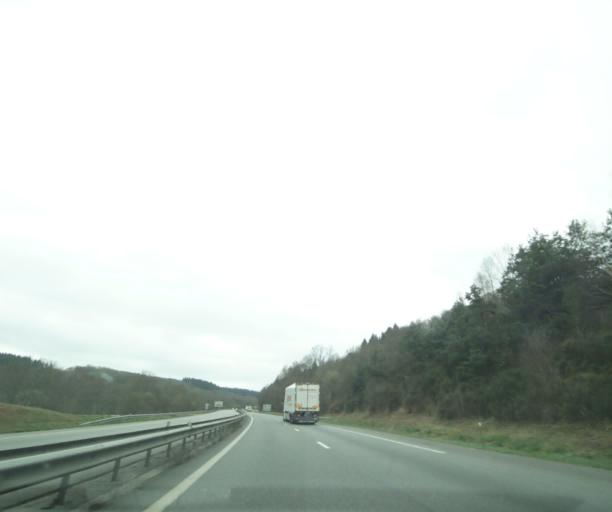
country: FR
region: Limousin
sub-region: Departement de la Haute-Vienne
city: Razes
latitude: 46.0375
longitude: 1.3494
